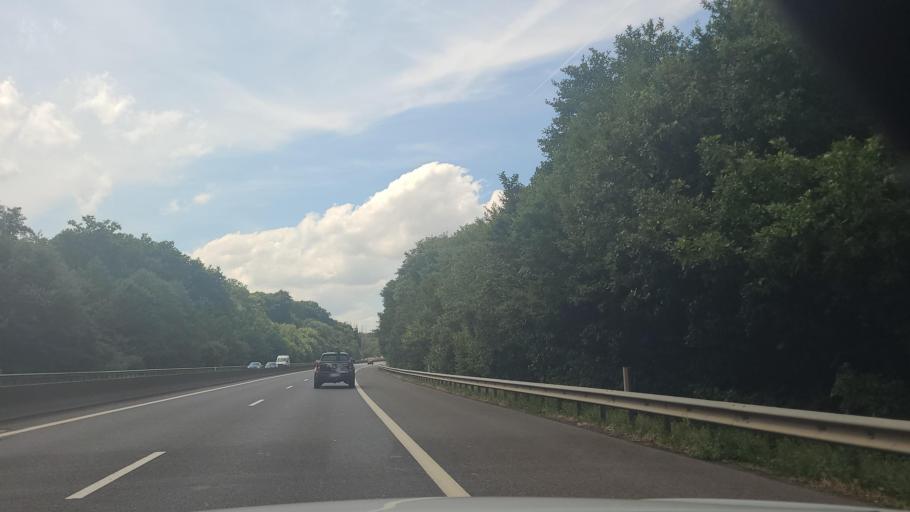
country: LU
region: Luxembourg
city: Capellen
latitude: 49.6350
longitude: 5.9892
